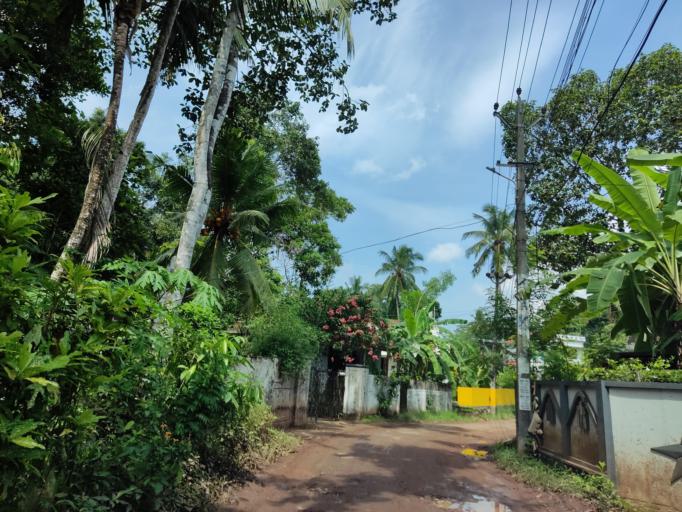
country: IN
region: Kerala
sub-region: Alappuzha
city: Mavelikara
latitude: 9.2600
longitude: 76.5638
